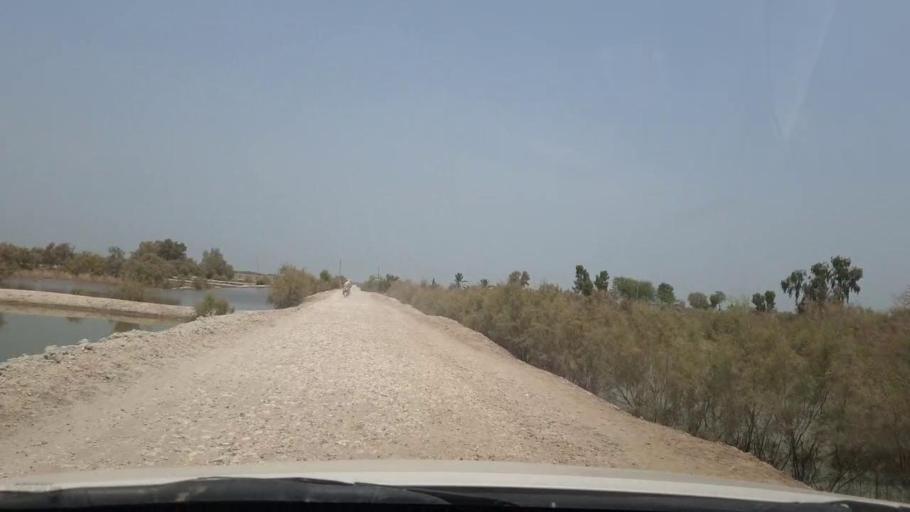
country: PK
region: Sindh
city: Rustam jo Goth
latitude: 28.0584
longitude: 68.8163
